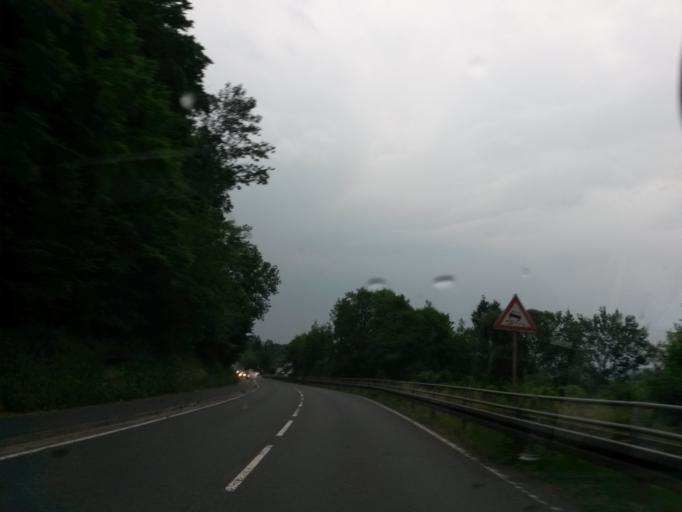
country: DE
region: North Rhine-Westphalia
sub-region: Regierungsbezirk Koln
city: Overath
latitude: 50.9519
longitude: 7.3099
